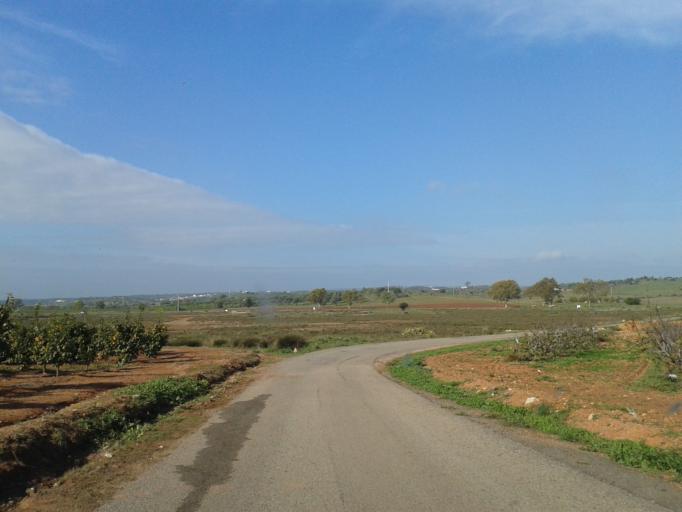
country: PT
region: Faro
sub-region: Vila Real de Santo Antonio
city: Monte Gordo
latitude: 37.2002
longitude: -7.4751
